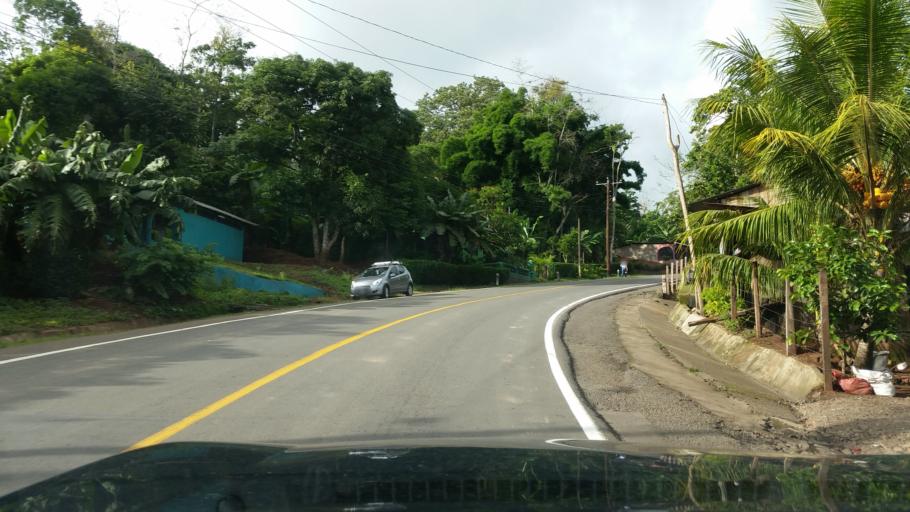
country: NI
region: Matagalpa
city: San Ramon
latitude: 13.1320
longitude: -85.7388
